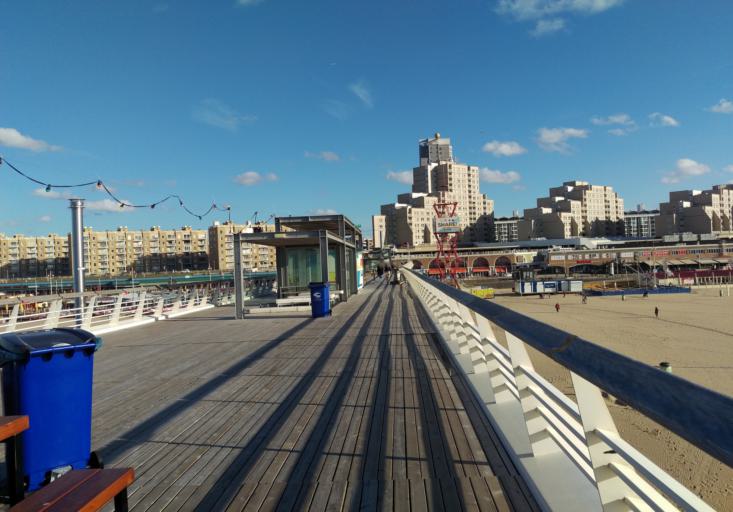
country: NL
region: South Holland
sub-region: Gemeente Den Haag
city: Scheveningen
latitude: 52.1165
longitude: 4.2813
